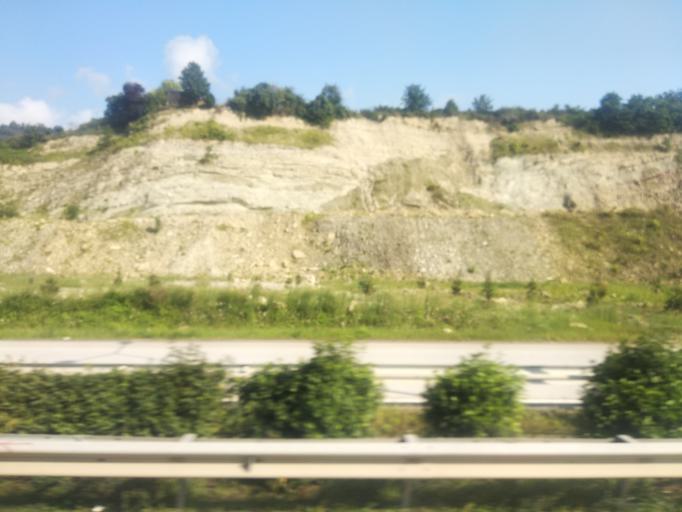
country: TR
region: Ordu
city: Ordu
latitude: 41.0011
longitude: 37.8236
